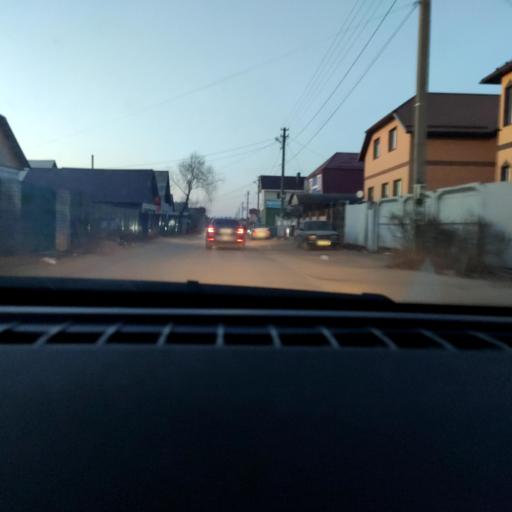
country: RU
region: Voronezj
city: Podgornoye
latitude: 51.7418
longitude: 39.1641
